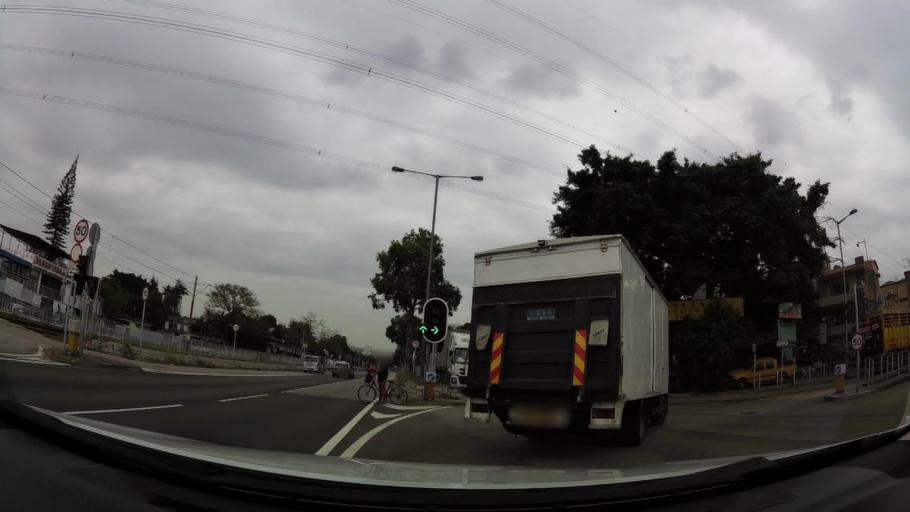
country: HK
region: Tuen Mun
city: Tuen Mun
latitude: 22.4263
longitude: 113.9891
